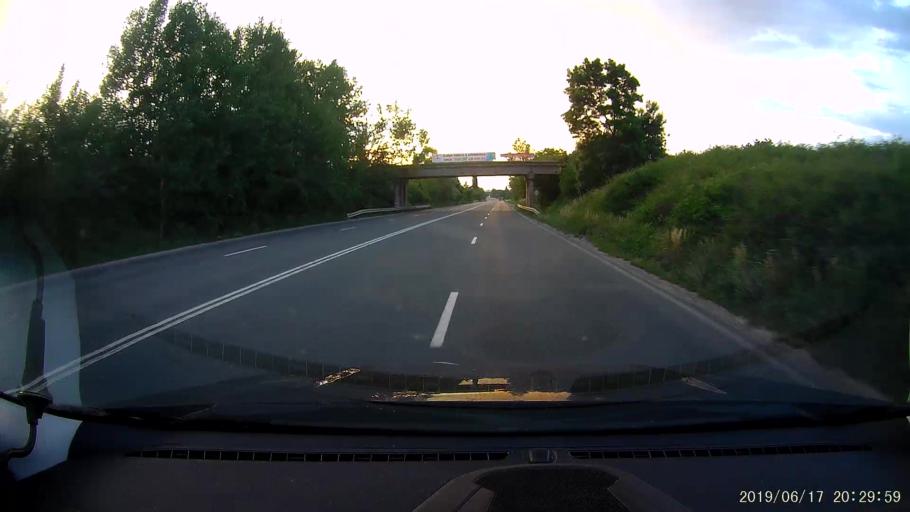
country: BG
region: Sofiya
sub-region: Obshtina Bozhurishte
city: Bozhurishte
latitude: 42.7915
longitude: 23.1517
